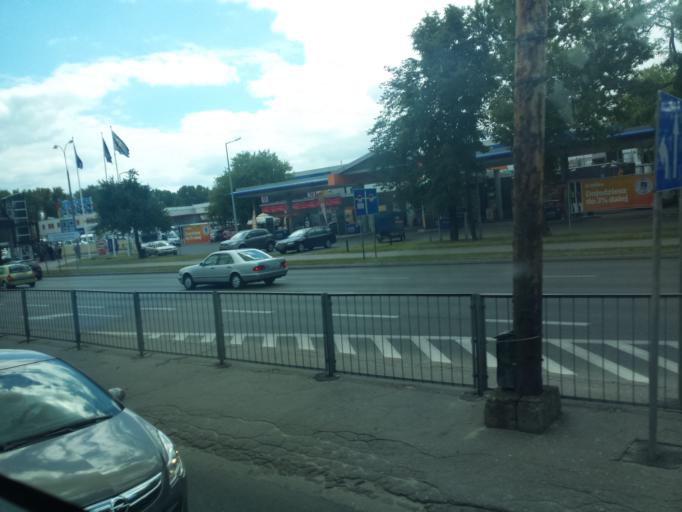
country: PL
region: Masovian Voivodeship
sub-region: Warszawa
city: Praga Poludnie
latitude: 52.2378
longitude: 21.1190
